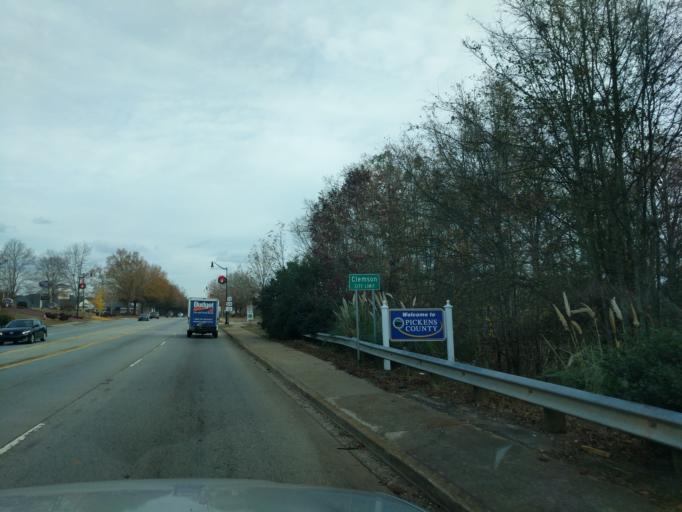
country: US
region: South Carolina
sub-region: Pickens County
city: Clemson
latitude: 34.6927
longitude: -82.8548
